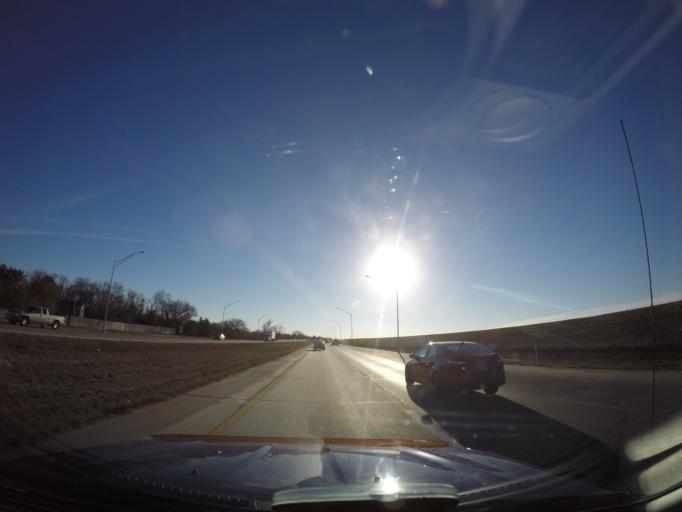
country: US
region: Kansas
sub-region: Sedgwick County
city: Wichita
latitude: 37.7292
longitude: -97.3832
